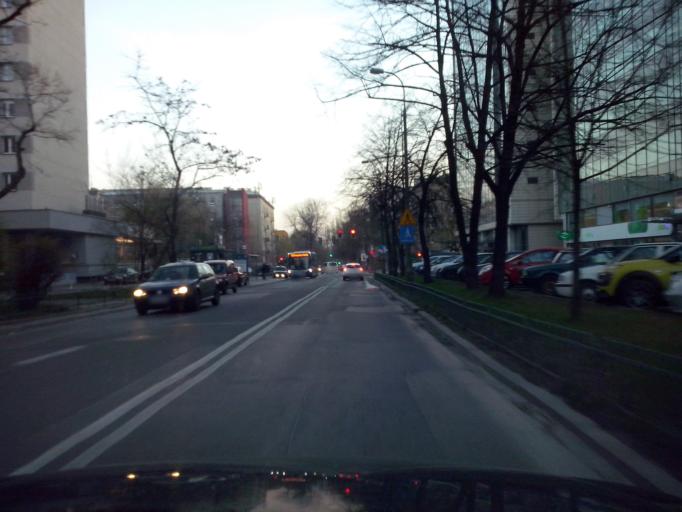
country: PL
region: Lesser Poland Voivodeship
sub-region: Krakow
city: Krakow
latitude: 50.0741
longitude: 19.9163
